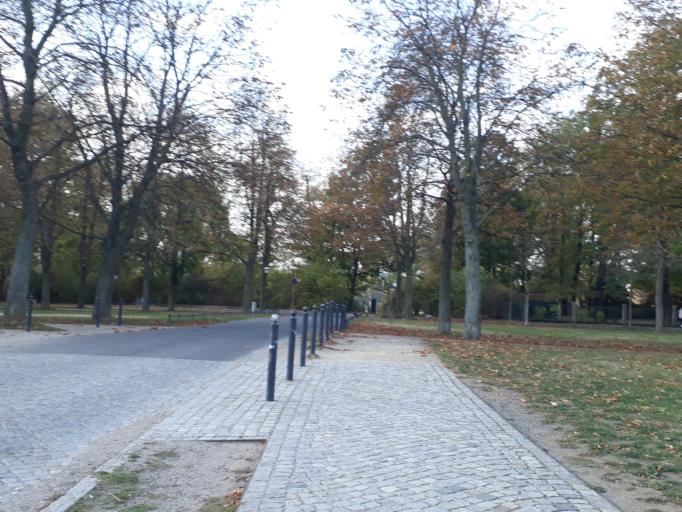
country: DE
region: Saxony
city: Heidenau
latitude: 51.0127
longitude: 13.8645
